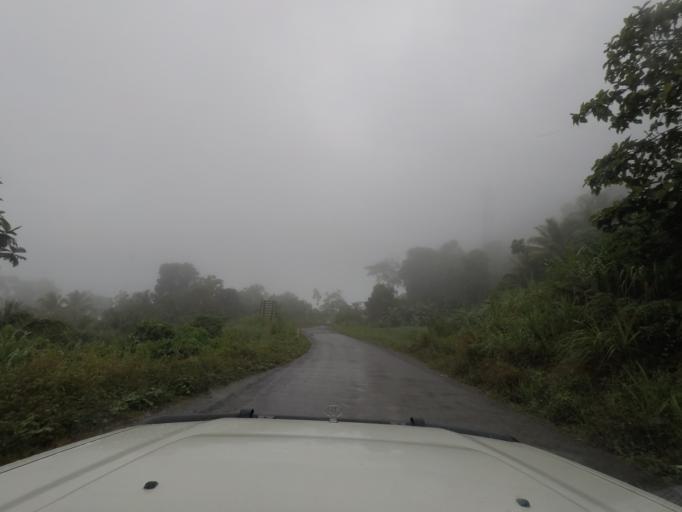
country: PG
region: Madang
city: Madang
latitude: -5.4512
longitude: 145.5088
